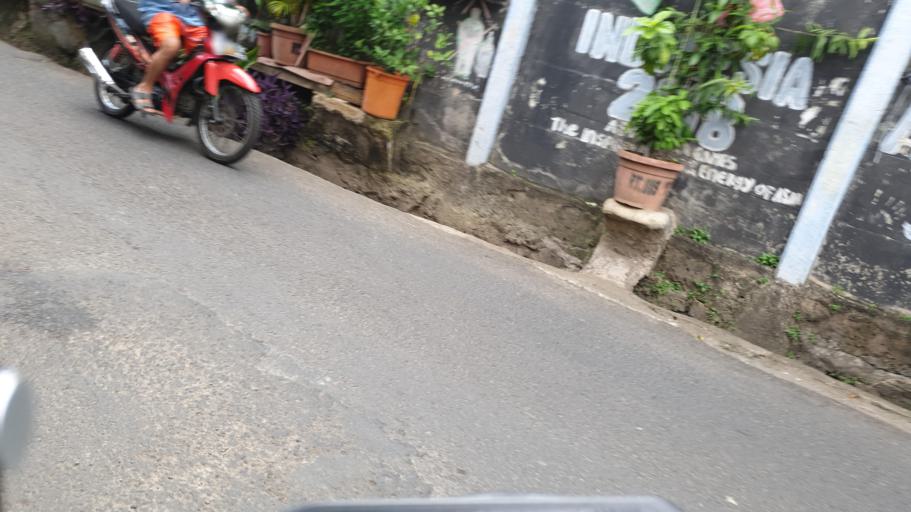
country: ID
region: Banten
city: South Tangerang
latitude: -6.2770
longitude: 106.7915
